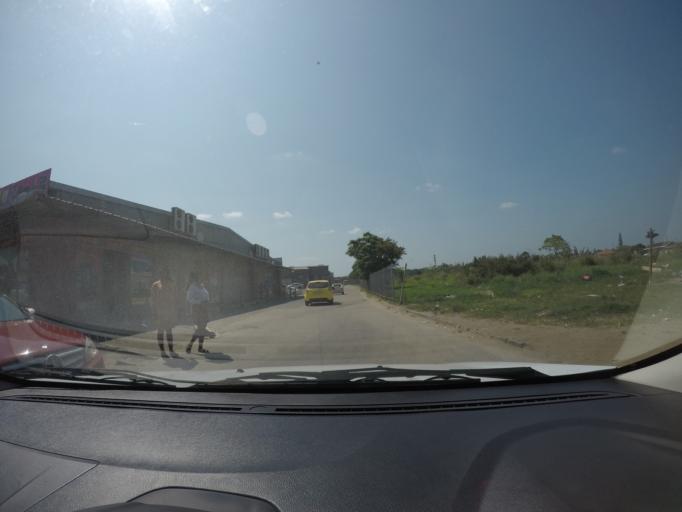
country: ZA
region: KwaZulu-Natal
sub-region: uThungulu District Municipality
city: eSikhawini
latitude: -28.8734
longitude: 31.8988
